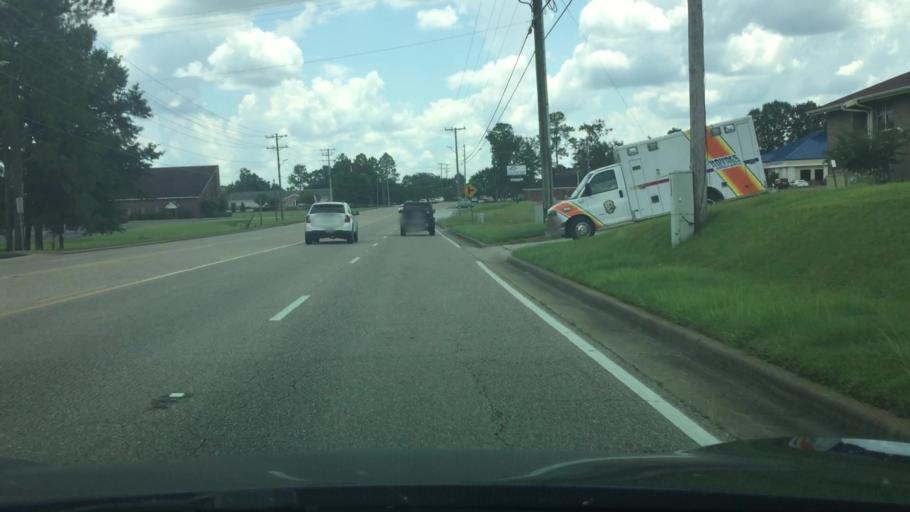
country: US
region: Alabama
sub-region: Pike County
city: Troy
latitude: 31.7781
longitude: -85.9626
